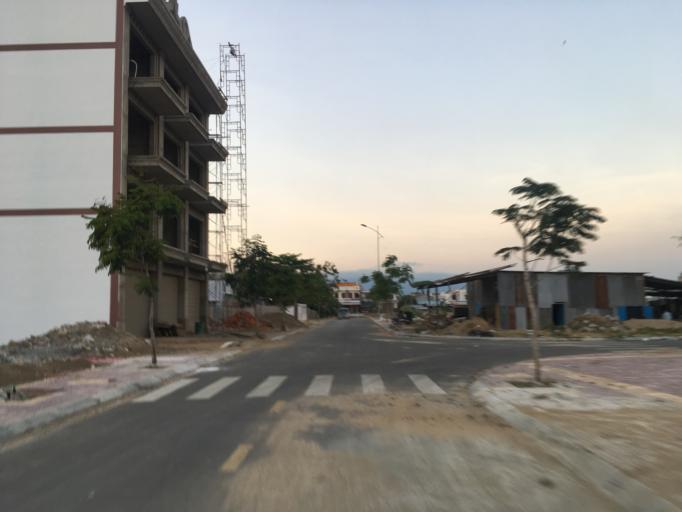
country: VN
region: Ninh Thuan
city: Phan Rang-Thap Cham
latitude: 11.5705
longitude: 108.9954
